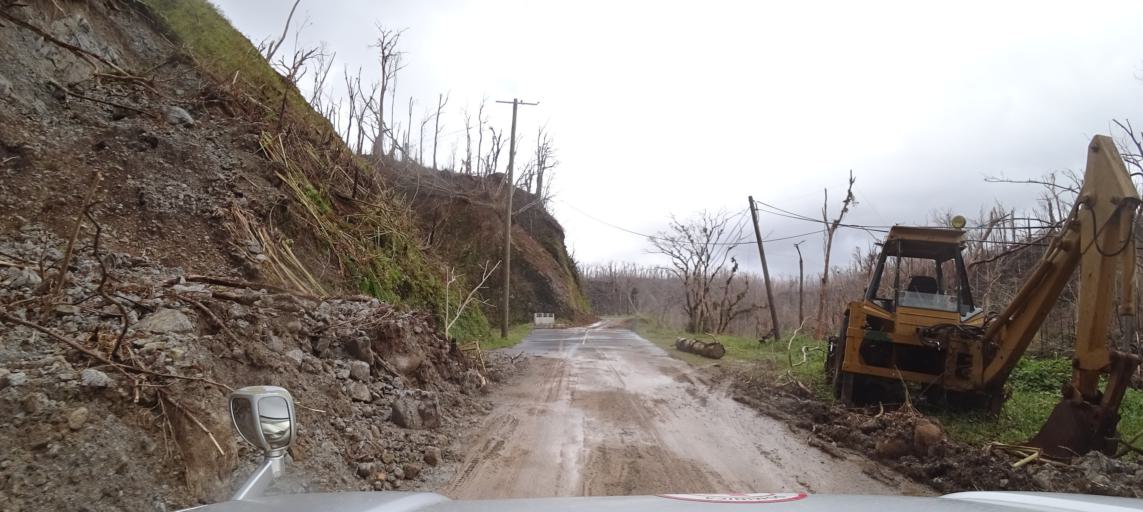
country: DM
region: Saint Paul
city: Pont Casse
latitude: 15.4293
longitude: -61.3341
